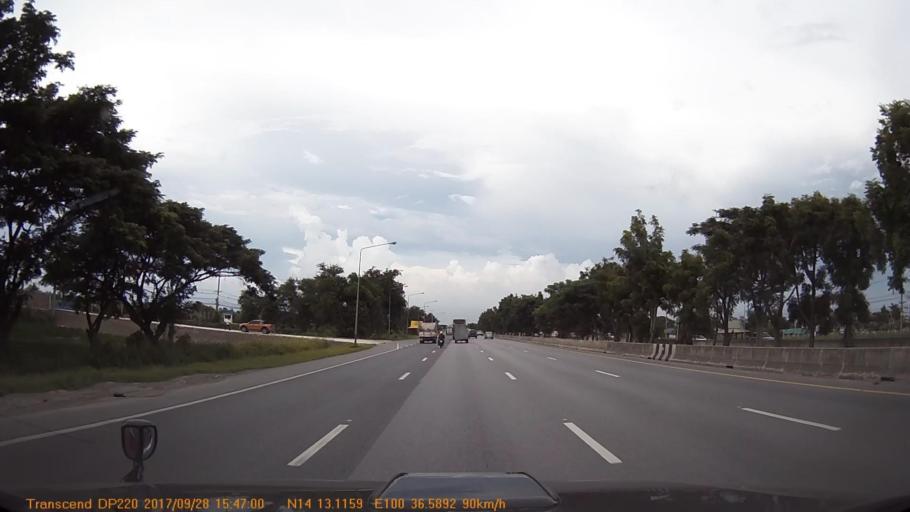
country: TH
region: Phra Nakhon Si Ayutthaya
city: Bang Pa-in
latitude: 14.2189
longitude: 100.6099
